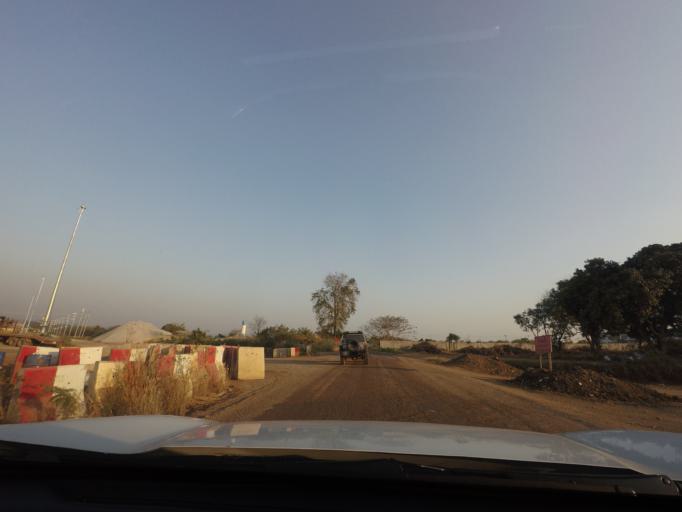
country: TH
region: Nakhon Ratchasima
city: Pak Chong
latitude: 14.6445
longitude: 101.4026
